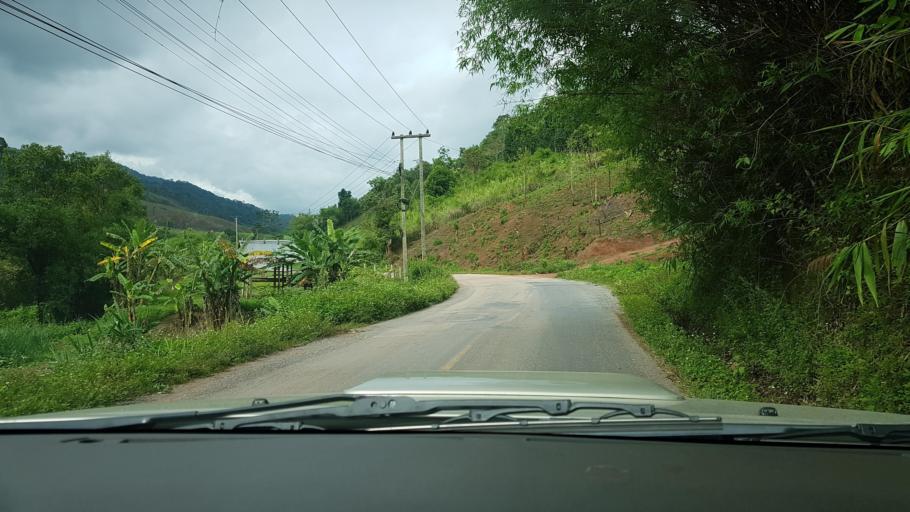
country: LA
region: Oudomxai
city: Muang Xay
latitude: 20.5665
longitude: 101.9199
